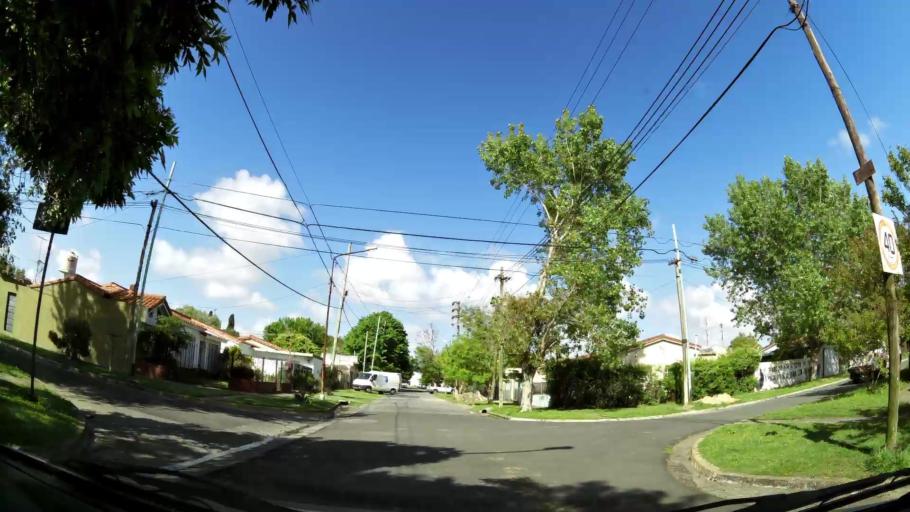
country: AR
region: Buenos Aires
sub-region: Partido de Quilmes
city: Quilmes
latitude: -34.7878
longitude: -58.1521
